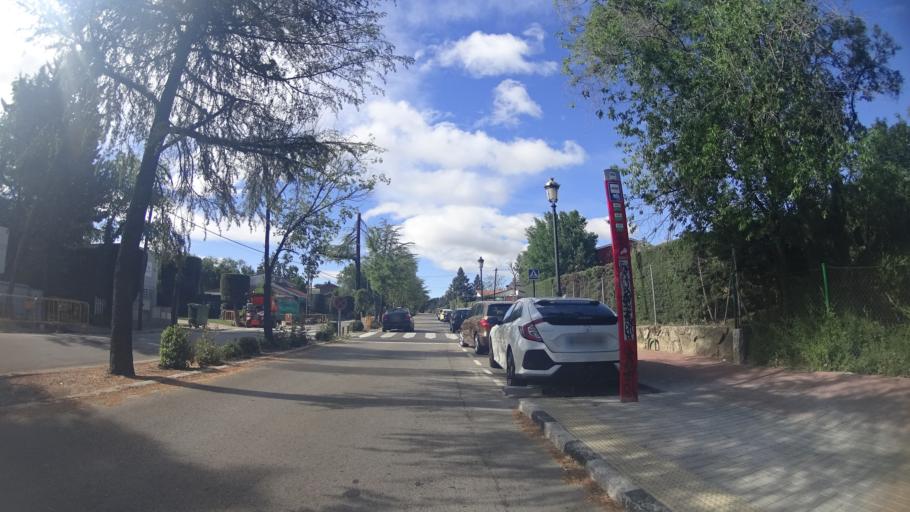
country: ES
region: Madrid
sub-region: Provincia de Madrid
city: Villanueva del Pardillo
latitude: 40.4832
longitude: -3.9379
